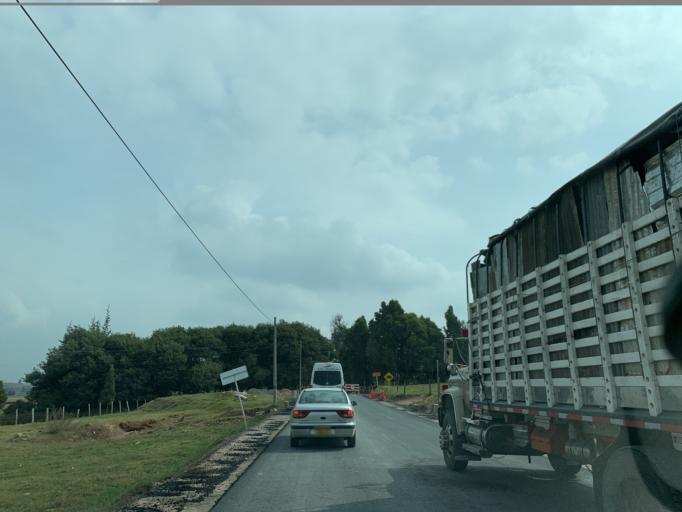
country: CO
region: Boyaca
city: Tunja
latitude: 5.5350
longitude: -73.3070
